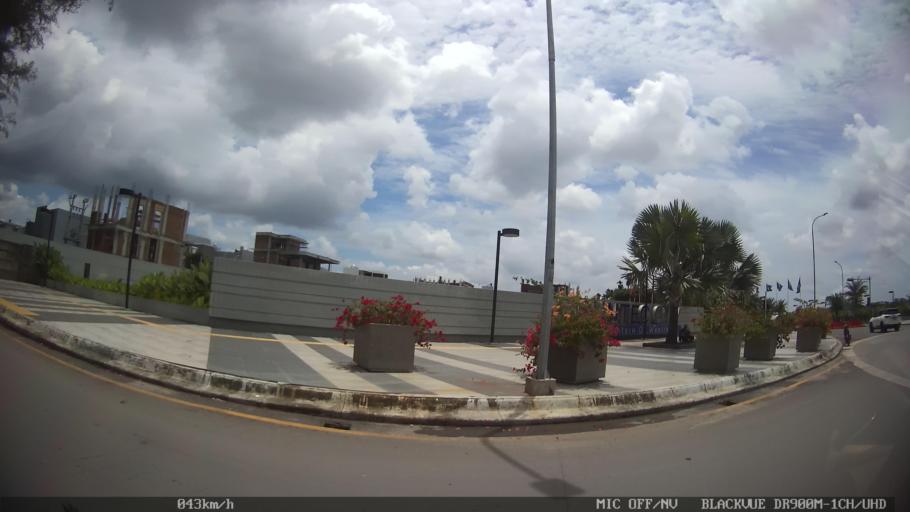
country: ID
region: North Sumatra
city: Medan
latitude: 3.6087
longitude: 98.7291
